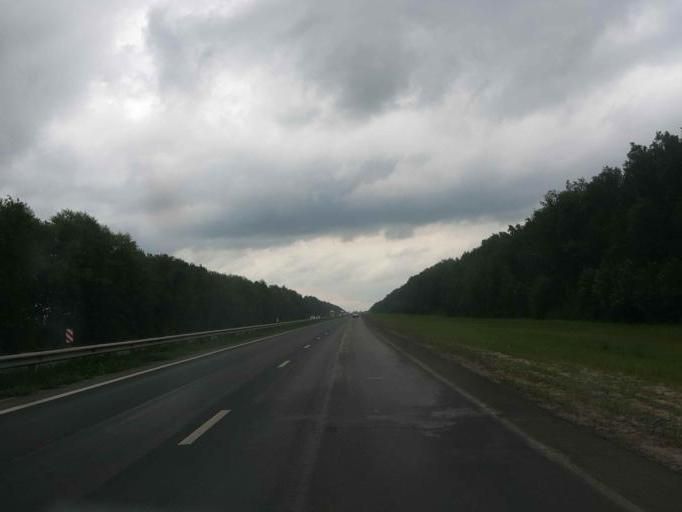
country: RU
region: Tambov
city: Selezni
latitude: 52.7661
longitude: 41.1022
